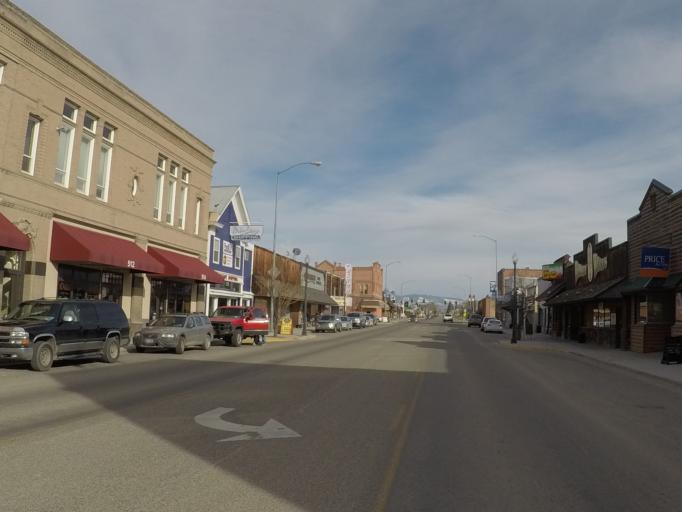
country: US
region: Idaho
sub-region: Lemhi County
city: Salmon
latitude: 45.1757
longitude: -113.8943
